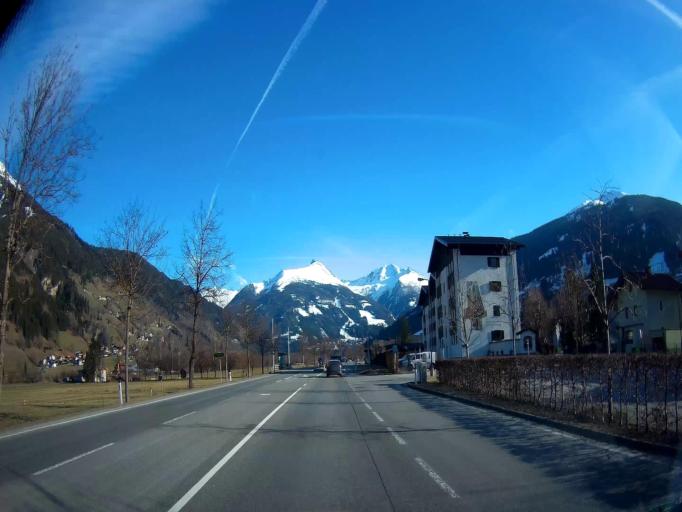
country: AT
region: Salzburg
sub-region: Politischer Bezirk Sankt Johann im Pongau
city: Bad Hofgastein
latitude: 47.1550
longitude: 13.1106
